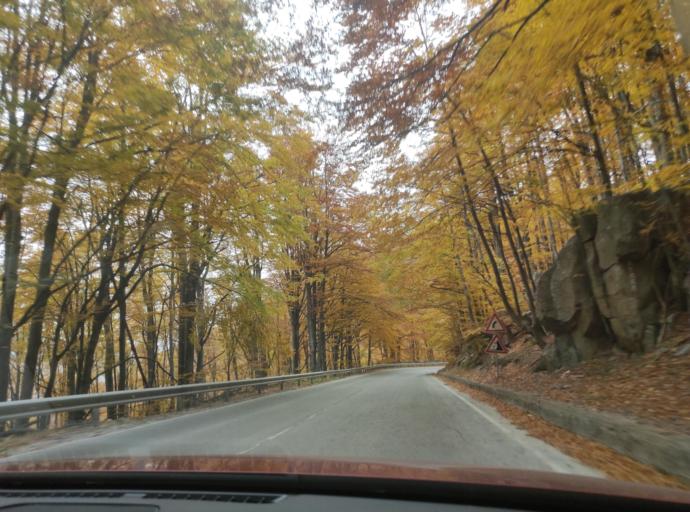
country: BG
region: Montana
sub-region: Obshtina Berkovitsa
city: Berkovitsa
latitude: 43.1345
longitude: 23.1456
